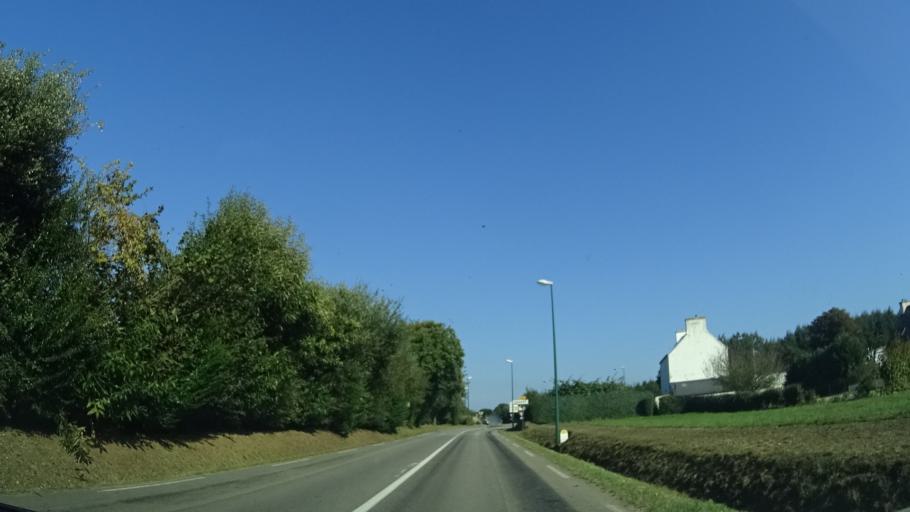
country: FR
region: Brittany
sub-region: Departement du Finistere
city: Plonevez-Porzay
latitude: 48.0915
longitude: -4.2667
